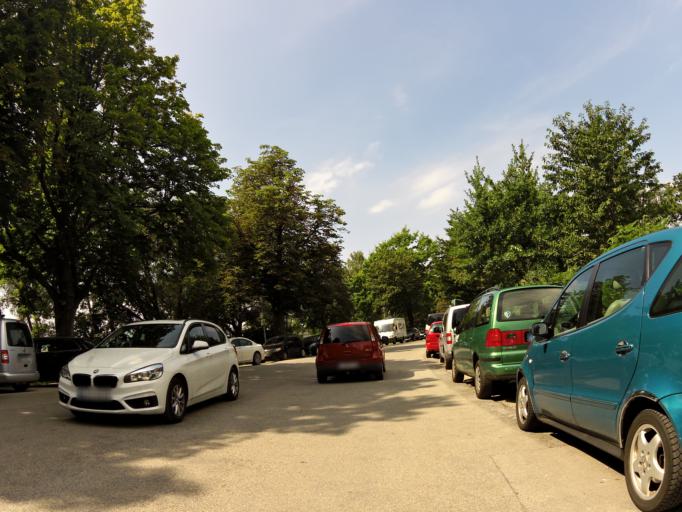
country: DE
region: Bavaria
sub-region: Upper Bavaria
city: Inning am Ammersee
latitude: 48.0762
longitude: 11.1355
